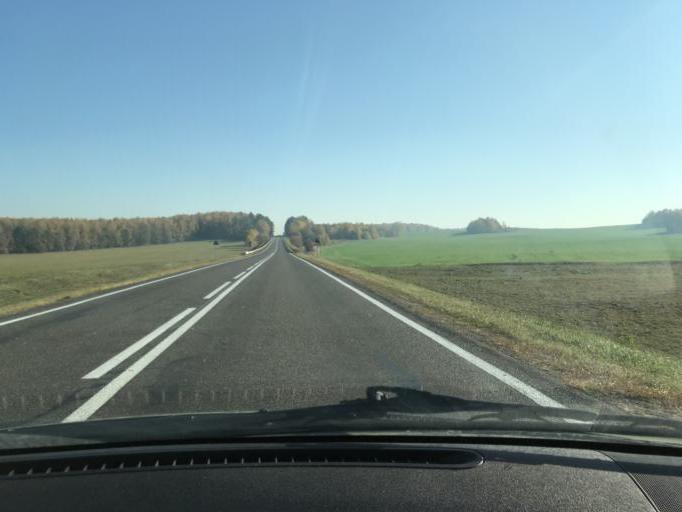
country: BY
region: Minsk
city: Klyetsk
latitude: 52.9685
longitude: 26.6048
